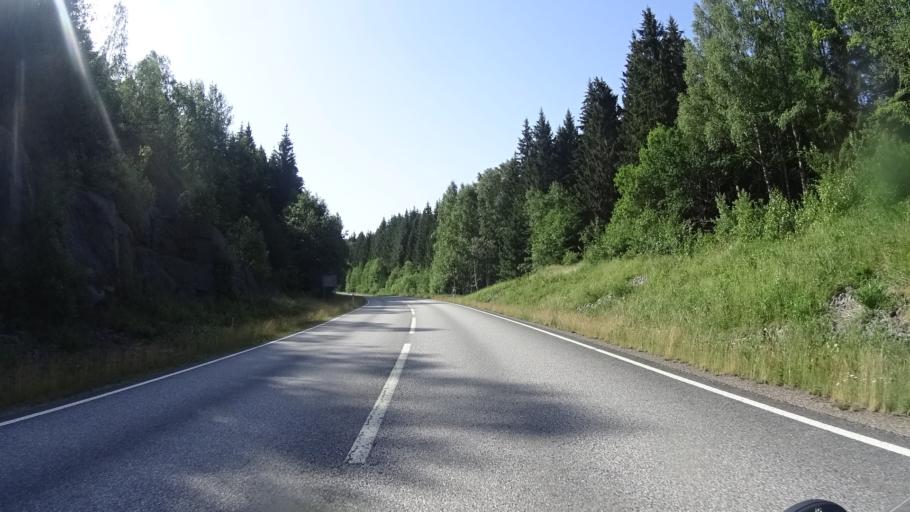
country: SE
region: Kalmar
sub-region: Vasterviks Kommun
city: Overum
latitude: 58.0527
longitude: 16.2035
